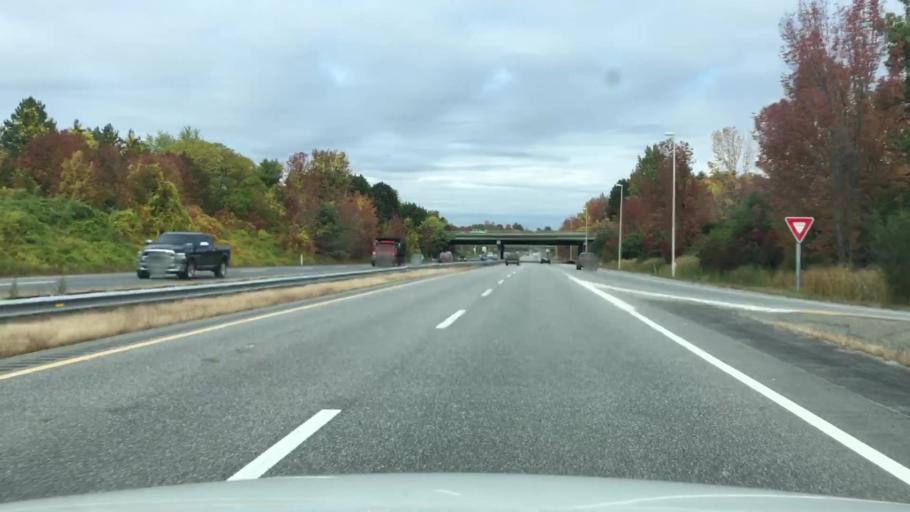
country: US
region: Maine
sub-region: Kennebec County
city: Augusta
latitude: 44.3145
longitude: -69.8106
